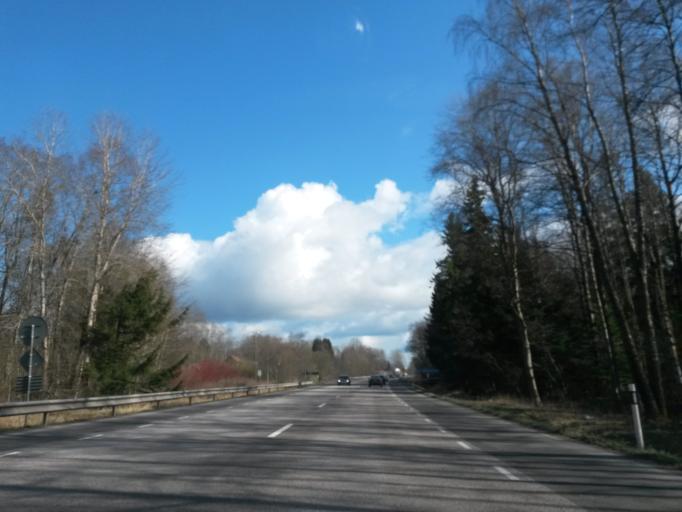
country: SE
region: Vaestra Goetaland
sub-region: Skovde Kommun
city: Skoevde
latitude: 58.3916
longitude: 13.7842
